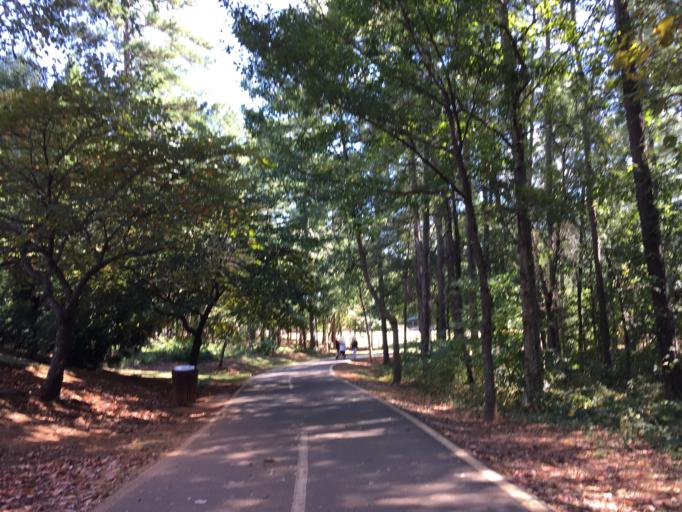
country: US
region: Georgia
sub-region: Fulton County
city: Alpharetta
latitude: 34.0171
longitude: -84.2668
